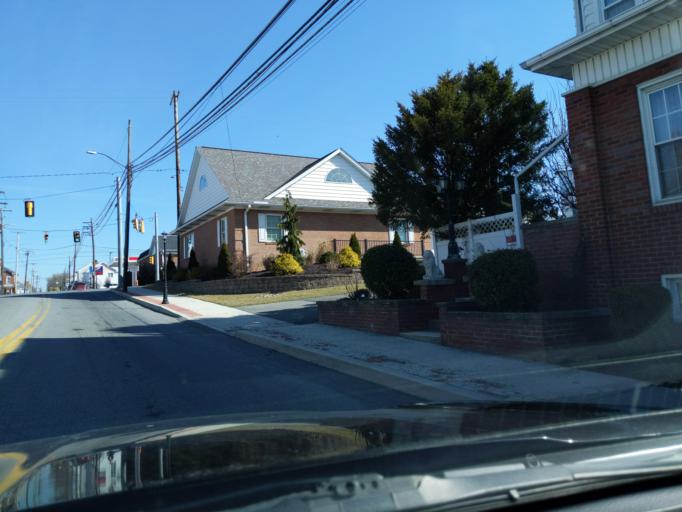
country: US
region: Pennsylvania
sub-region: Blair County
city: Martinsburg
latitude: 40.3109
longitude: -78.3253
